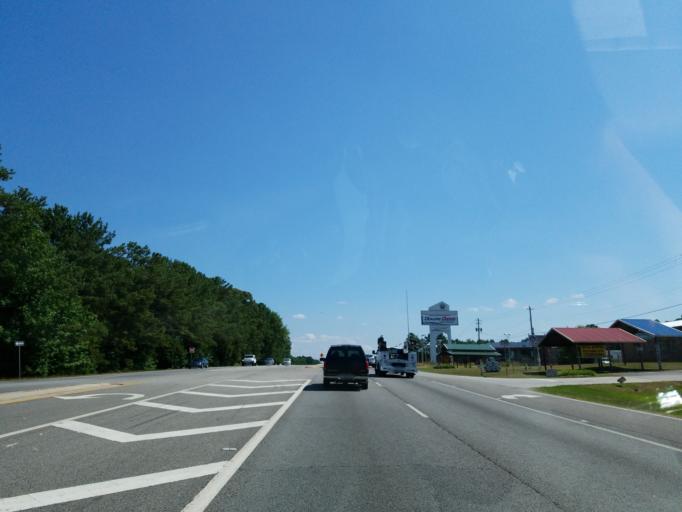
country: US
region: Georgia
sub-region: Spalding County
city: Experiment
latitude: 33.3001
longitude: -84.2915
